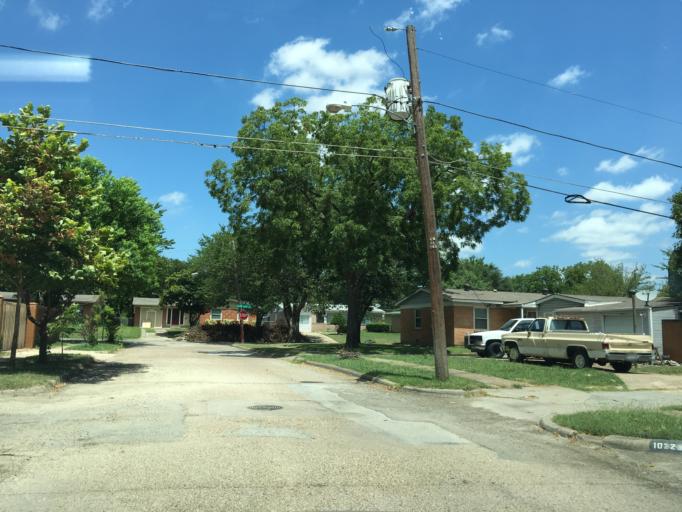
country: US
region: Texas
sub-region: Dallas County
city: Garland
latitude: 32.8357
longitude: -96.6609
